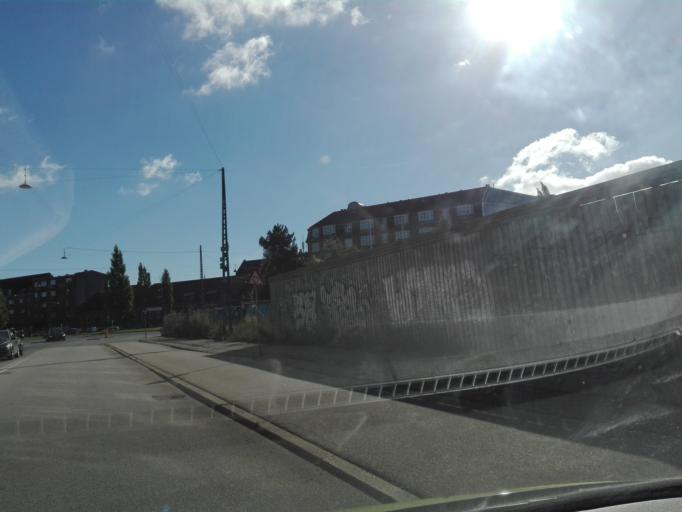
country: DK
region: Capital Region
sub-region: Kobenhavn
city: Christianshavn
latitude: 55.6678
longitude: 12.6108
